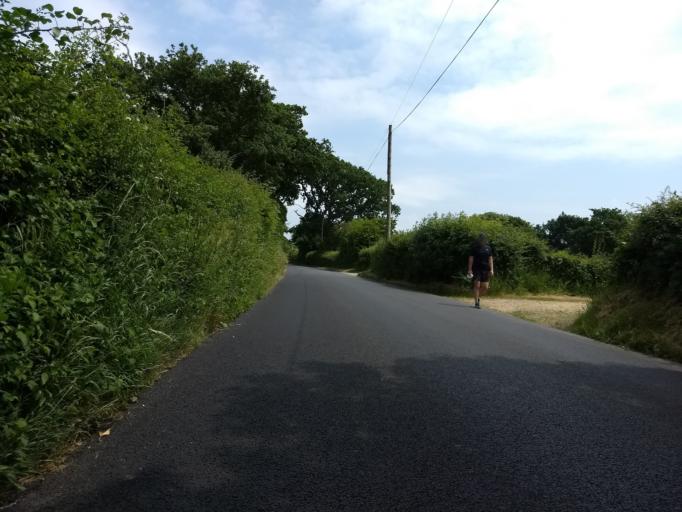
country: GB
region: England
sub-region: Isle of Wight
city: Seaview
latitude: 50.7133
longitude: -1.1357
